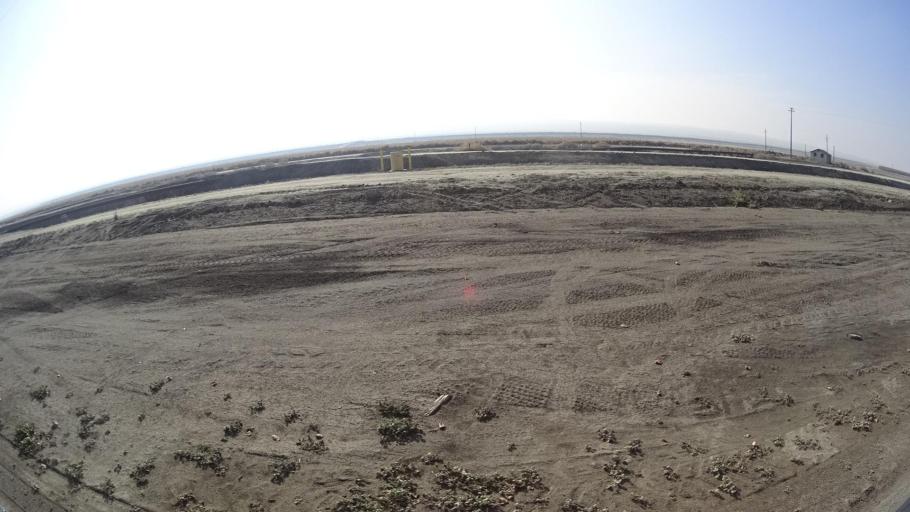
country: US
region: California
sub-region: Kern County
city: Buttonwillow
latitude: 35.3406
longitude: -119.4276
